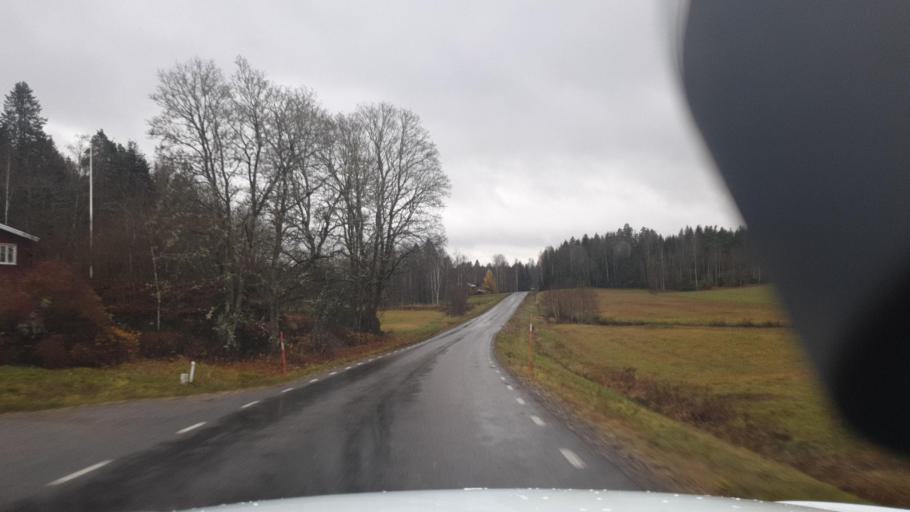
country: SE
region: Vaermland
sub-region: Eda Kommun
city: Charlottenberg
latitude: 59.8050
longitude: 12.1521
